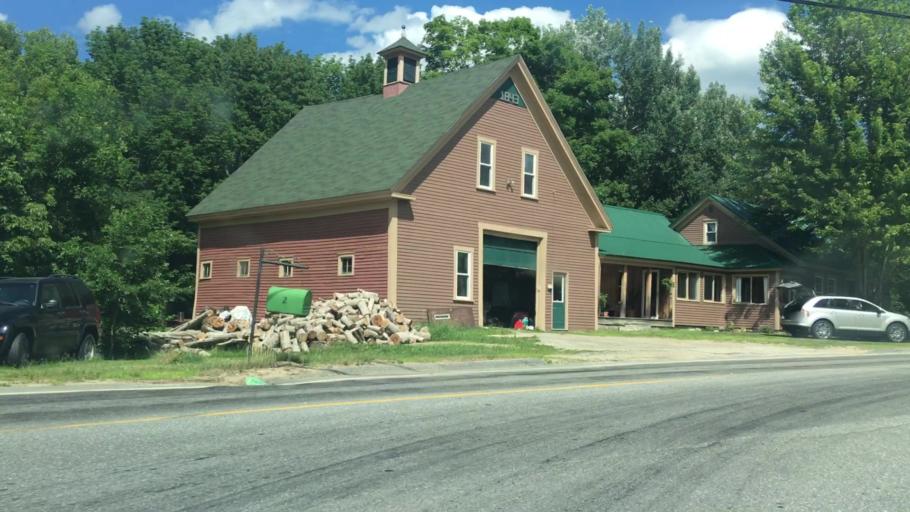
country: US
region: Maine
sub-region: Franklin County
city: Wilton
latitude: 44.5777
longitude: -70.1753
